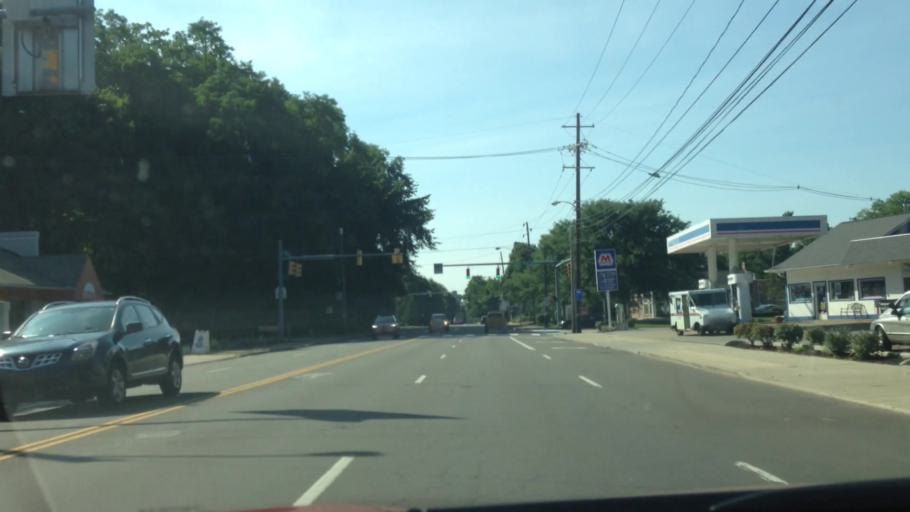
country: US
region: Ohio
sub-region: Summit County
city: Fairlawn
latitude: 41.1172
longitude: -81.5869
